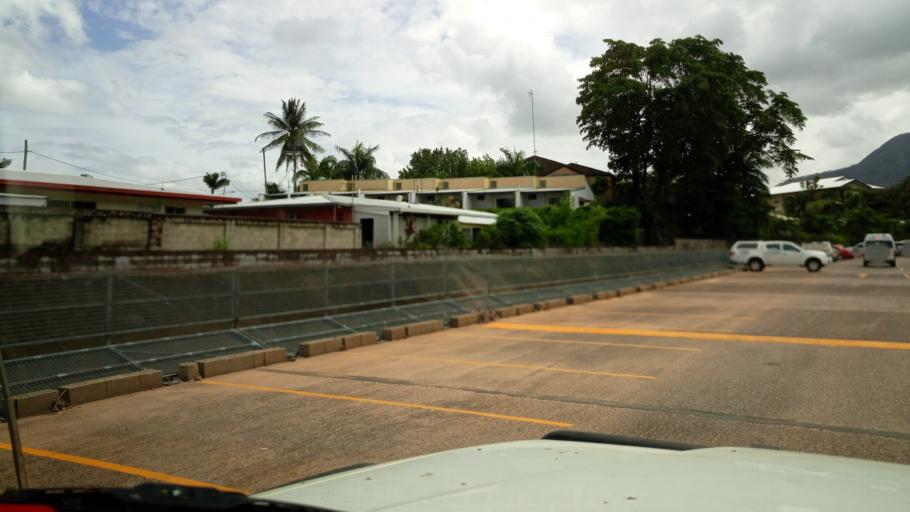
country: AU
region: Queensland
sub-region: Cairns
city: Woree
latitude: -16.9442
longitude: 145.7415
